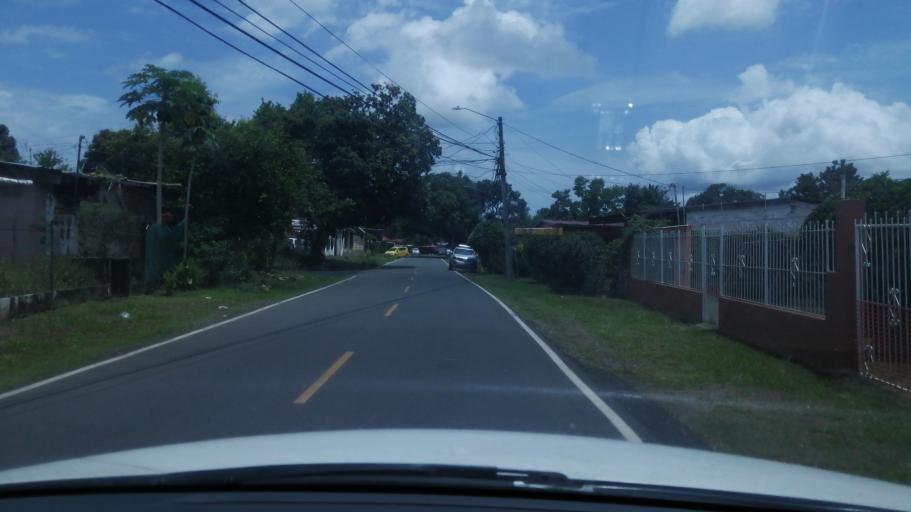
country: PA
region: Chiriqui
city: David
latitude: 8.4207
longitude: -82.4262
